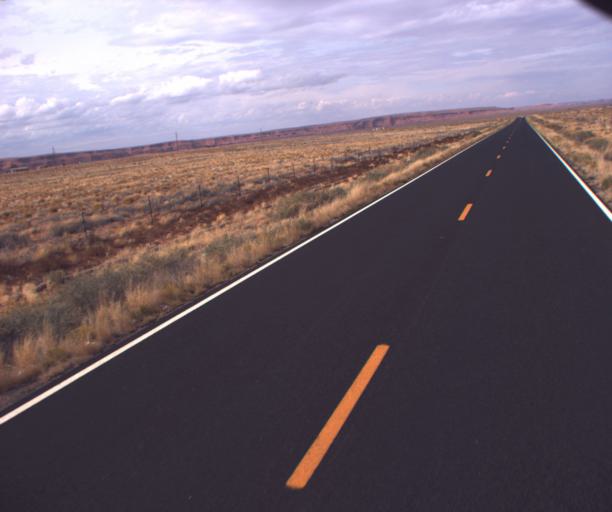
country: US
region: Arizona
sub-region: Apache County
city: Many Farms
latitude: 36.5556
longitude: -109.5352
